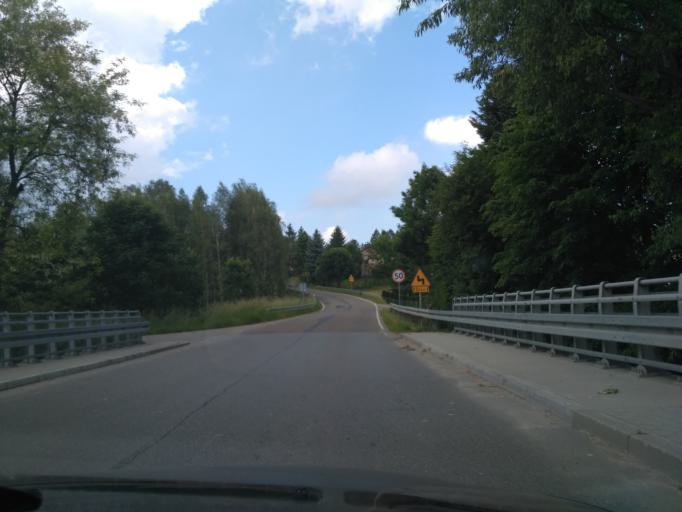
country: PL
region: Subcarpathian Voivodeship
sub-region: Powiat rzeszowski
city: Hyzne
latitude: 49.9549
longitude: 22.2017
